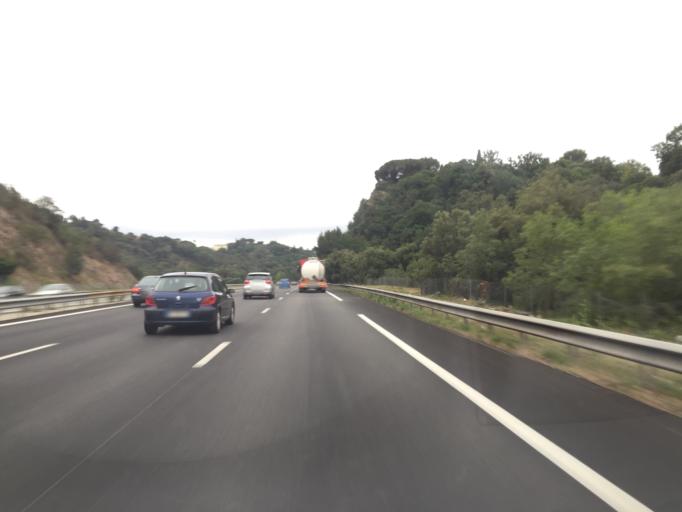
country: FR
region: Provence-Alpes-Cote d'Azur
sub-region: Departement des Alpes-Maritimes
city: La Roquette-sur-Siagne
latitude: 43.5669
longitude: 6.9733
